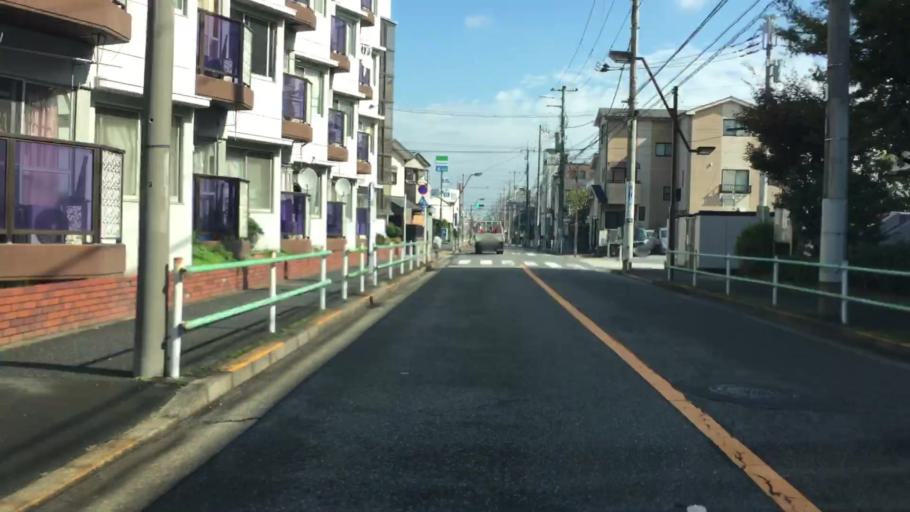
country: JP
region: Saitama
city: Yashio-shi
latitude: 35.7597
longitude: 139.8346
